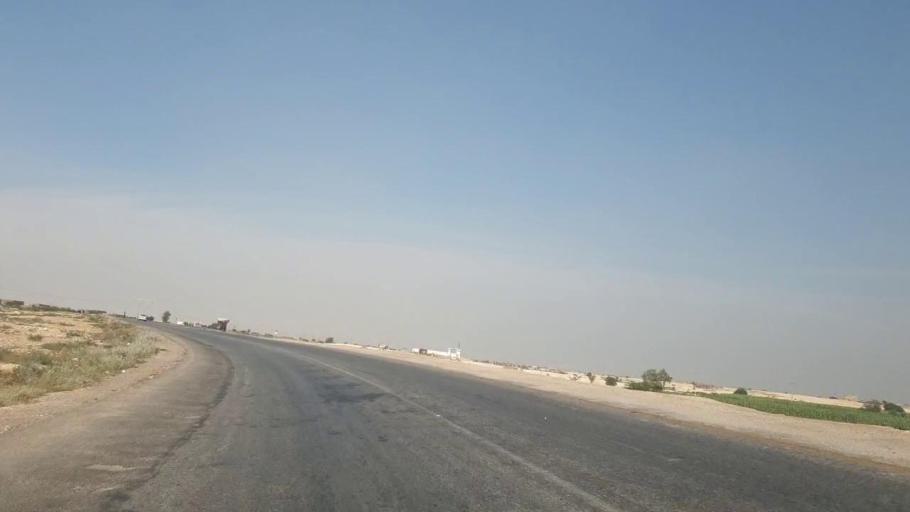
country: PK
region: Sindh
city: Hala
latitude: 25.7979
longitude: 68.2801
